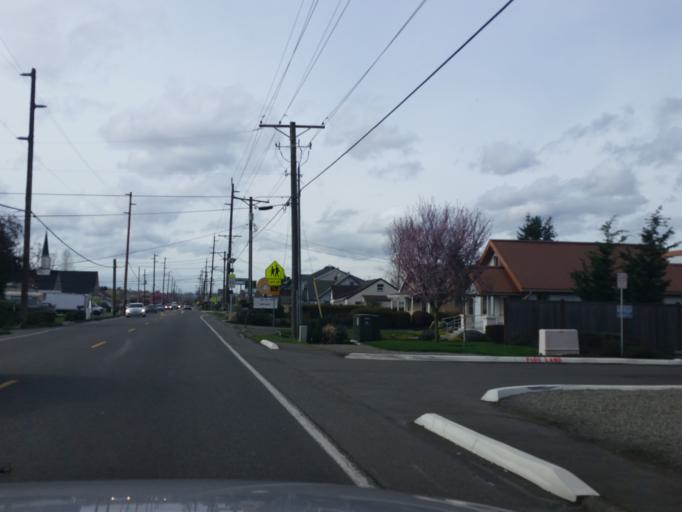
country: US
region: Washington
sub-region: Pierce County
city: Fife
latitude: 47.2390
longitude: -122.3451
